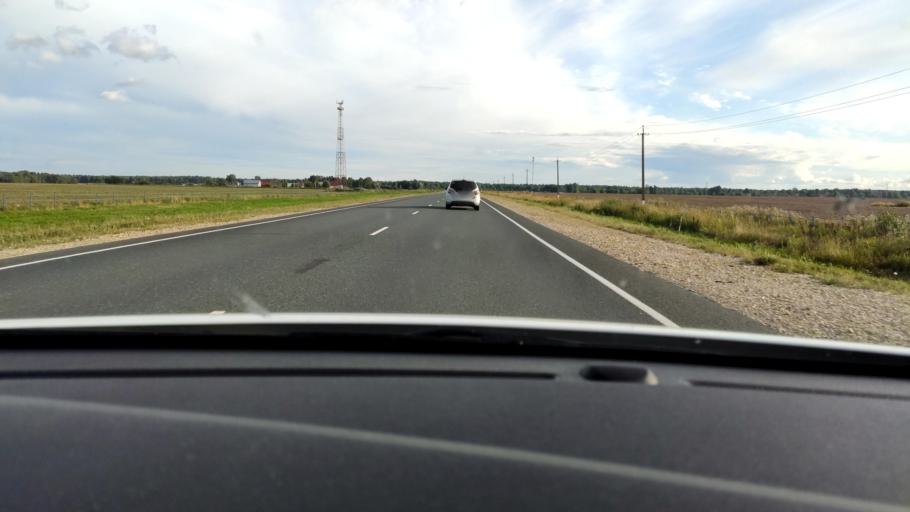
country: RU
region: Mariy-El
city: Krasnogorskiy
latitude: 56.2066
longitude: 48.2358
